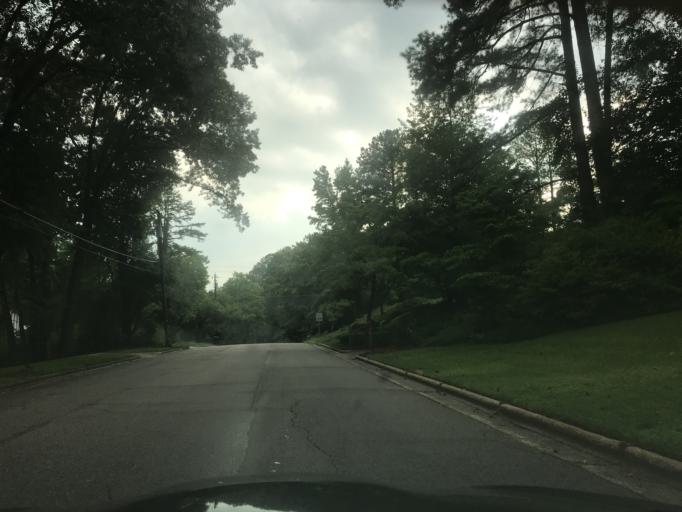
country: US
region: North Carolina
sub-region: Wake County
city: West Raleigh
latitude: 35.8356
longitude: -78.6570
